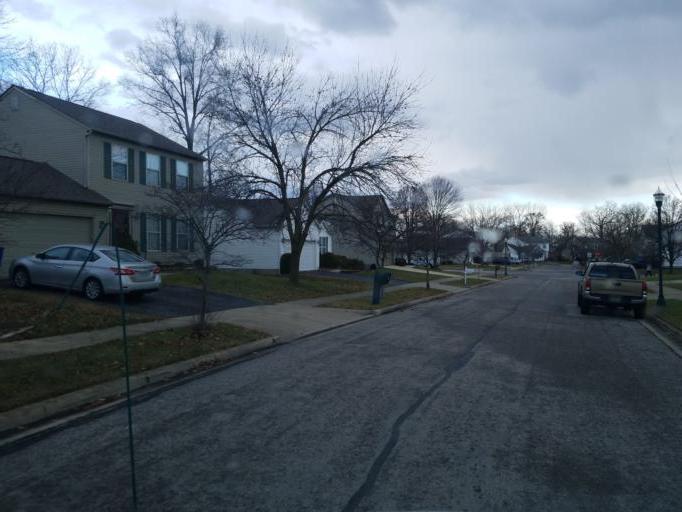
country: US
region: Ohio
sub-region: Delaware County
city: Delaware
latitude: 40.3170
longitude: -83.0958
